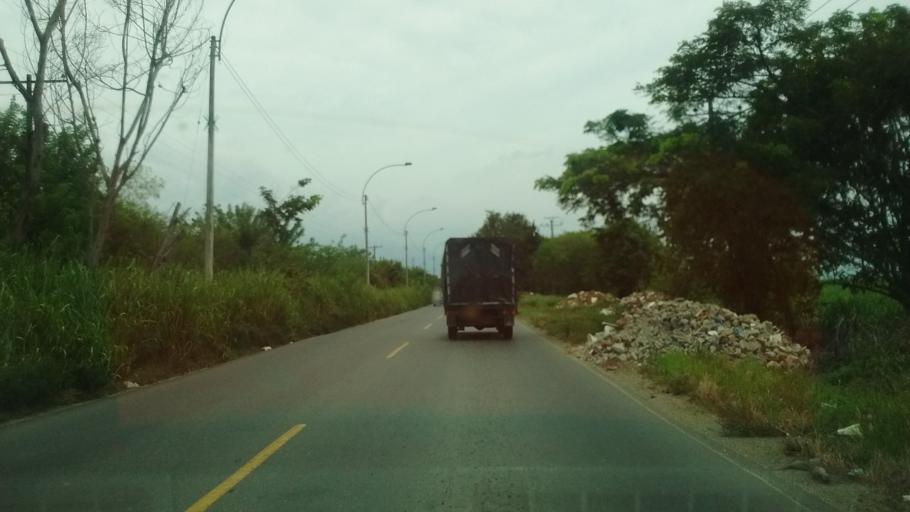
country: CO
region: Valle del Cauca
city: Jamundi
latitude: 3.3279
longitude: -76.5051
